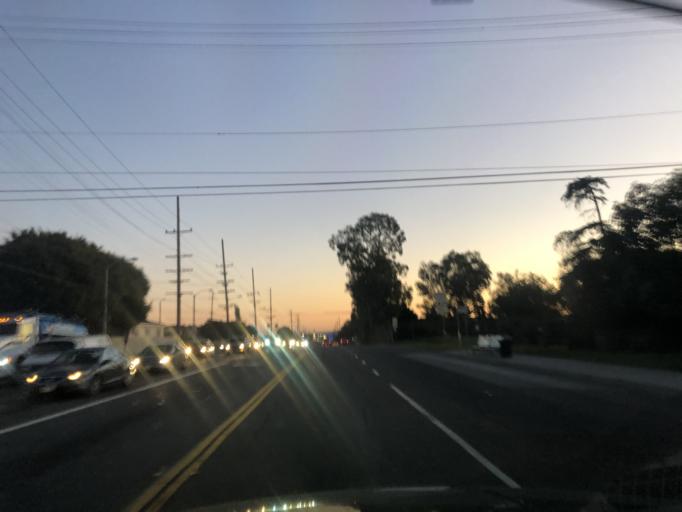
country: US
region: California
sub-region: Los Angeles County
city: West Athens
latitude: 33.9240
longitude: -118.3091
